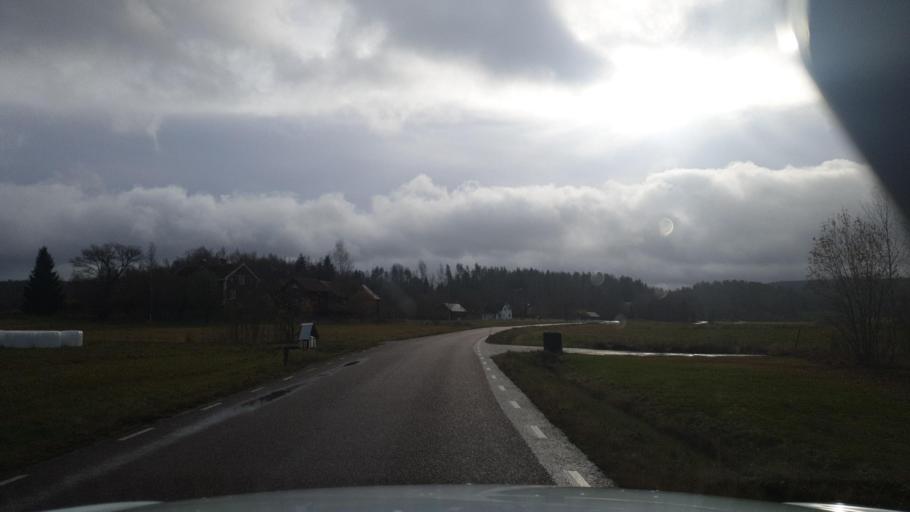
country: NO
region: Ostfold
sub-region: Romskog
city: Romskog
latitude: 59.7096
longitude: 12.0740
